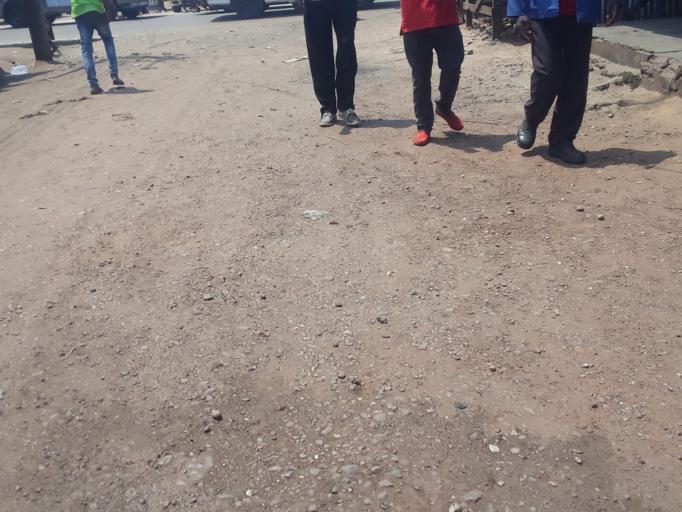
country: ZM
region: Lusaka
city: Lusaka
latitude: -15.3649
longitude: 28.2955
